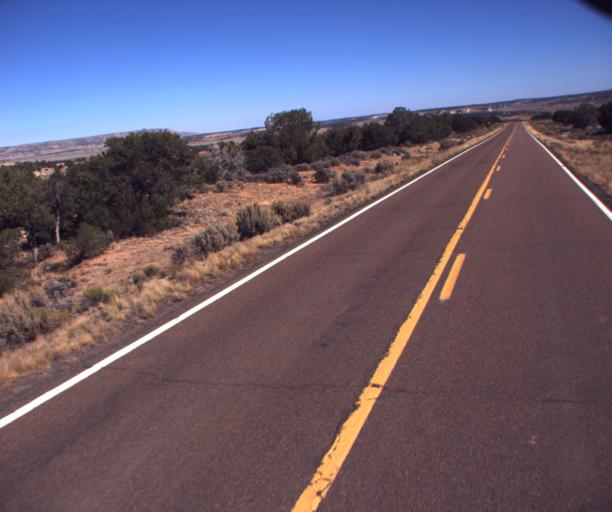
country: US
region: Arizona
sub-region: Apache County
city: Ganado
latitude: 35.7502
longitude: -109.9098
